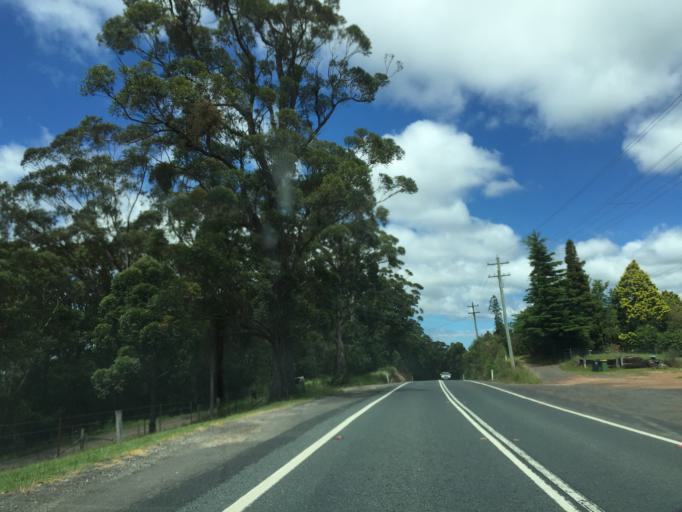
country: AU
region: New South Wales
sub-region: Blue Mountains Municipality
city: Hazelbrook
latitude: -33.5122
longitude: 150.4928
